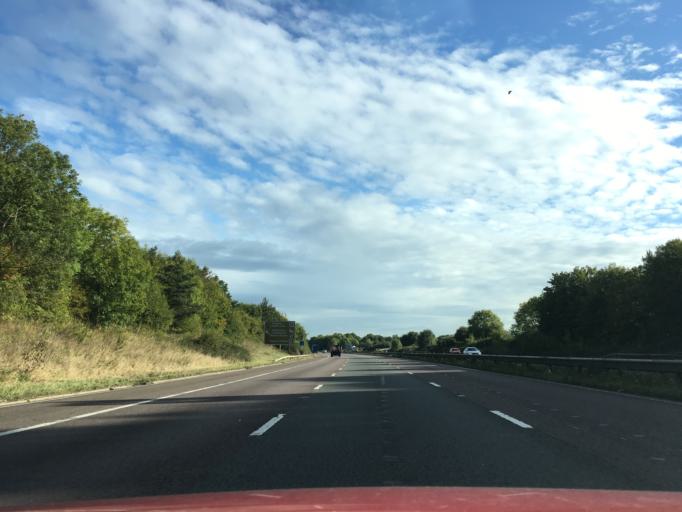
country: GB
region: England
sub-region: Gloucestershire
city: Churchdown
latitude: 51.8719
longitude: -2.1556
